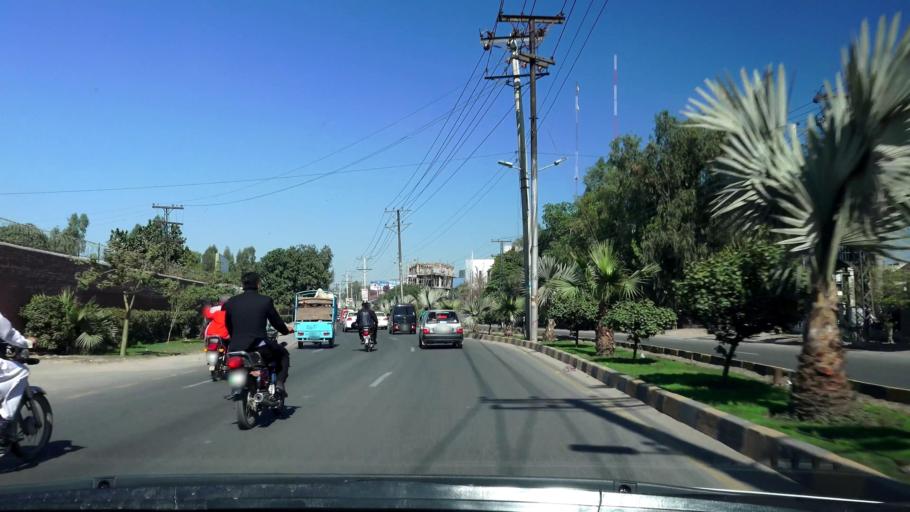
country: PK
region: Punjab
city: Faisalabad
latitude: 31.4319
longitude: 73.0782
